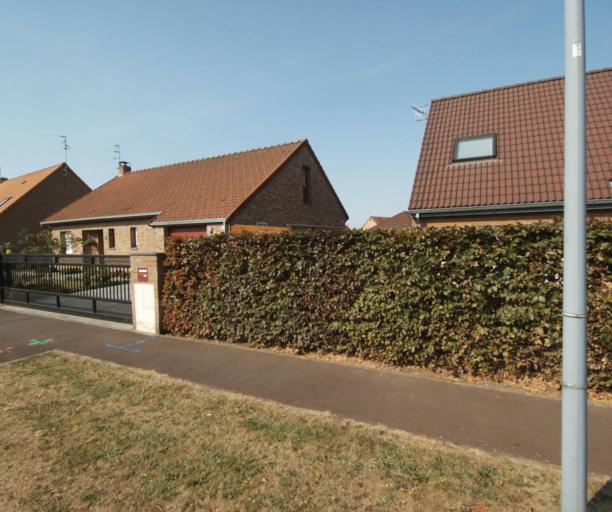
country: FR
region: Nord-Pas-de-Calais
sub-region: Departement du Nord
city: Comines
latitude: 50.7580
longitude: 2.9996
